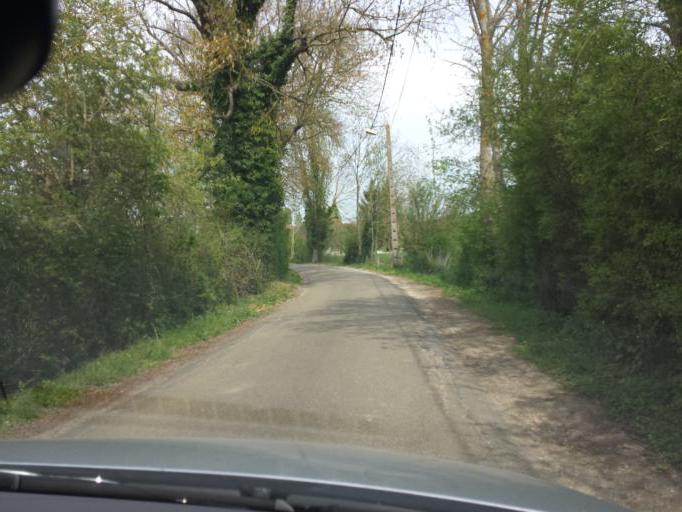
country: FR
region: Centre
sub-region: Departement d'Eure-et-Loir
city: Anet
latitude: 48.8500
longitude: 1.4576
